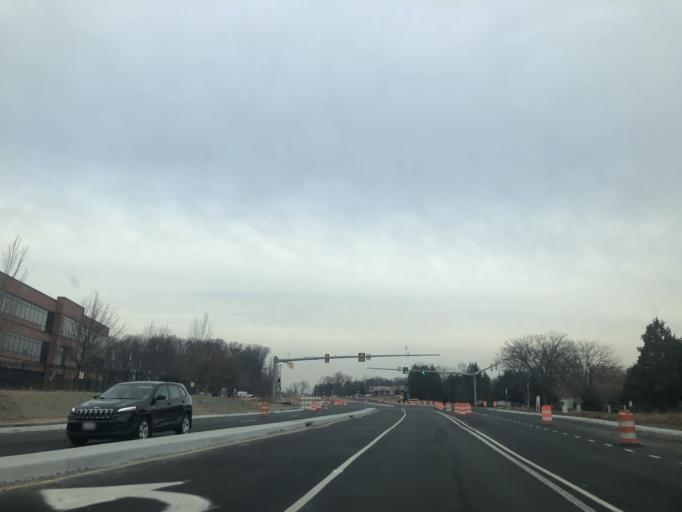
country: US
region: Virginia
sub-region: Loudoun County
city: Leesburg
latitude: 39.0815
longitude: -77.5529
